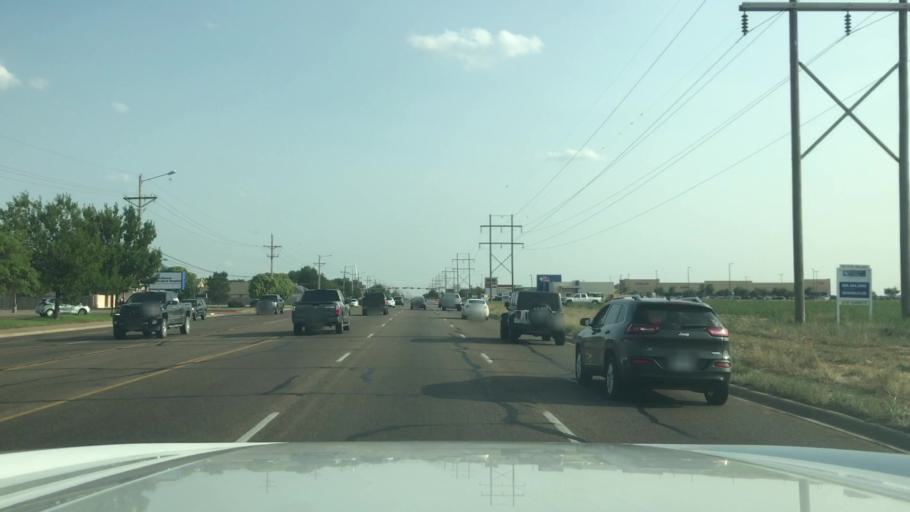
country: US
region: Texas
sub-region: Potter County
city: Amarillo
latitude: 35.1741
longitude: -101.9383
